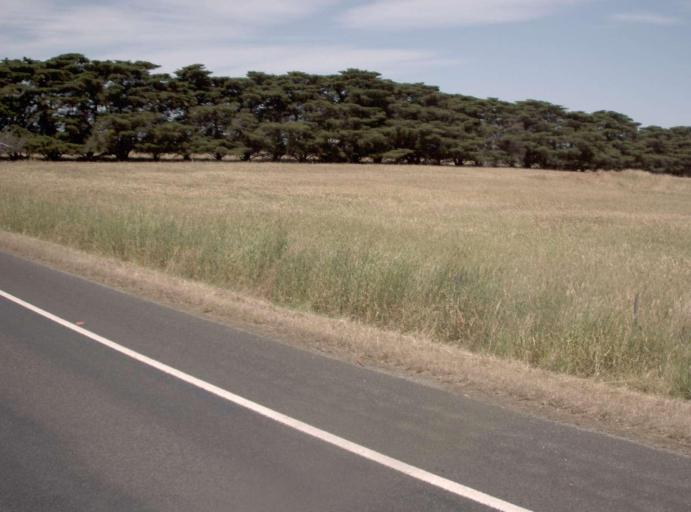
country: AU
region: Victoria
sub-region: Wellington
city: Heyfield
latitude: -38.1215
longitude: 146.8536
